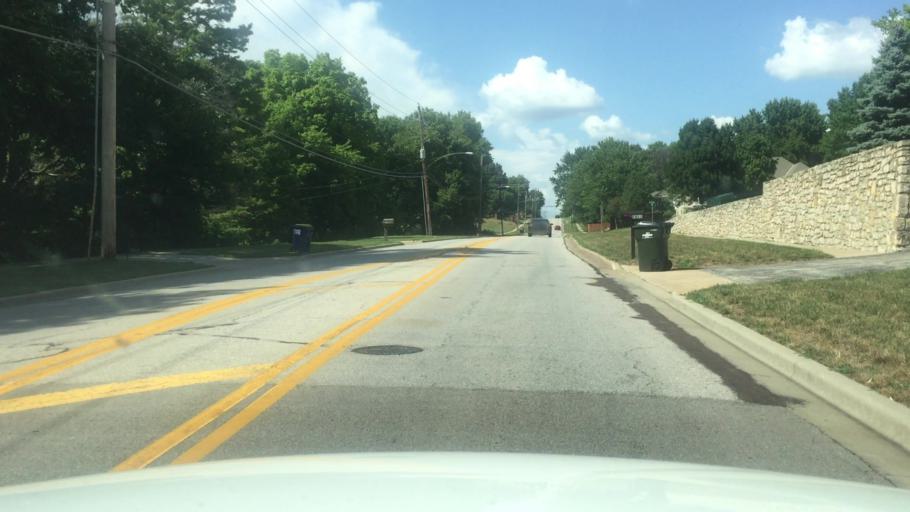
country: US
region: Kansas
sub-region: Johnson County
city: Shawnee
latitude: 39.0006
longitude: -94.7424
